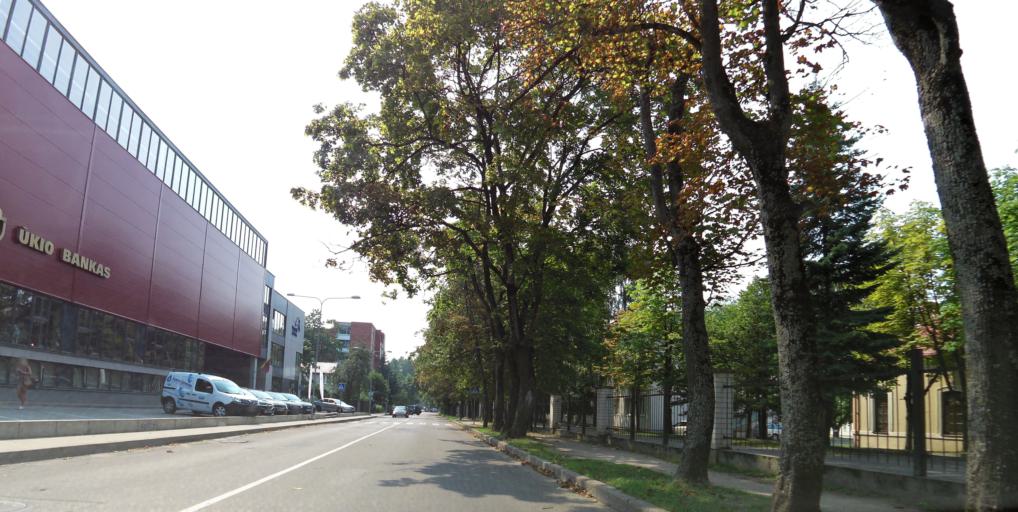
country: LT
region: Vilnius County
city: Rasos
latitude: 54.7021
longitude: 25.3149
